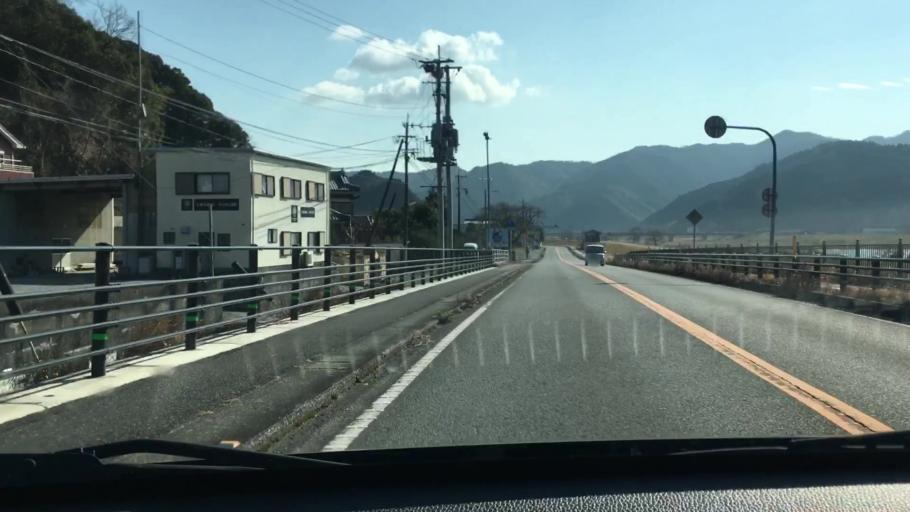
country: JP
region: Oita
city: Saiki
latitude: 32.9620
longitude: 131.8390
